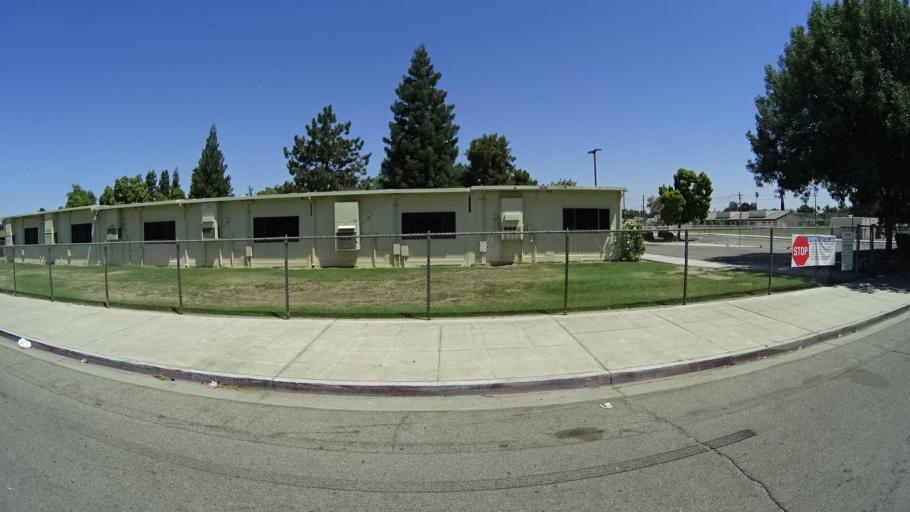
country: US
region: California
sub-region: Fresno County
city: Fresno
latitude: 36.7686
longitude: -119.7380
